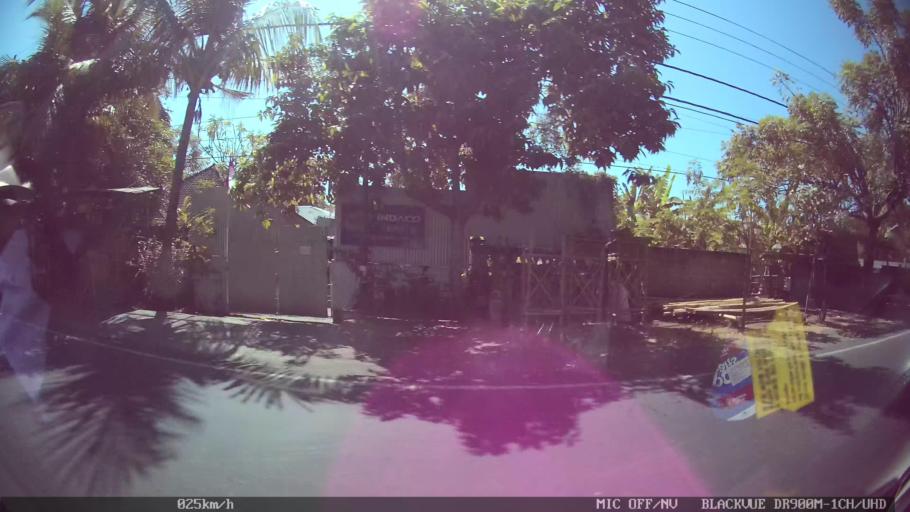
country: ID
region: Bali
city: Banjar Banyualit
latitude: -8.1514
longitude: 115.0428
